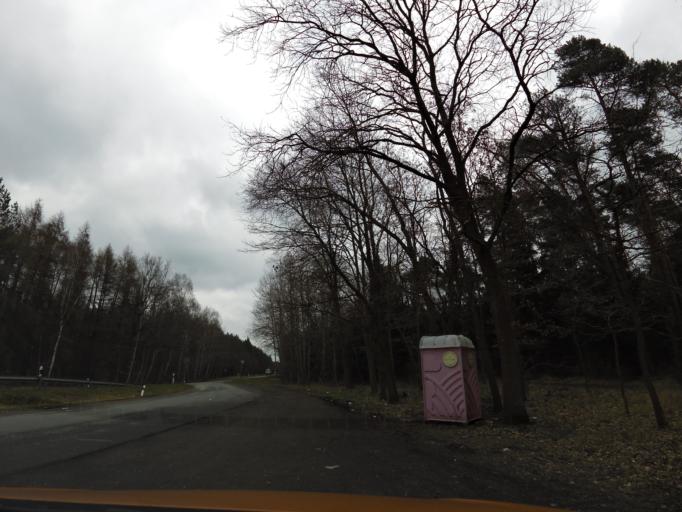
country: DE
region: Brandenburg
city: Rathenow
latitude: 52.6092
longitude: 12.4178
